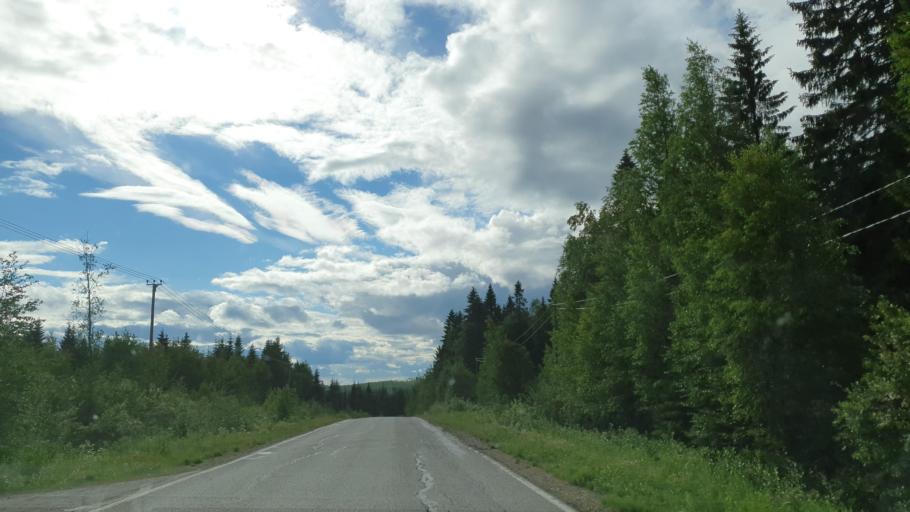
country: FI
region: Kainuu
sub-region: Kajaani
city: Ristijaervi
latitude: 64.3373
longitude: 28.0672
